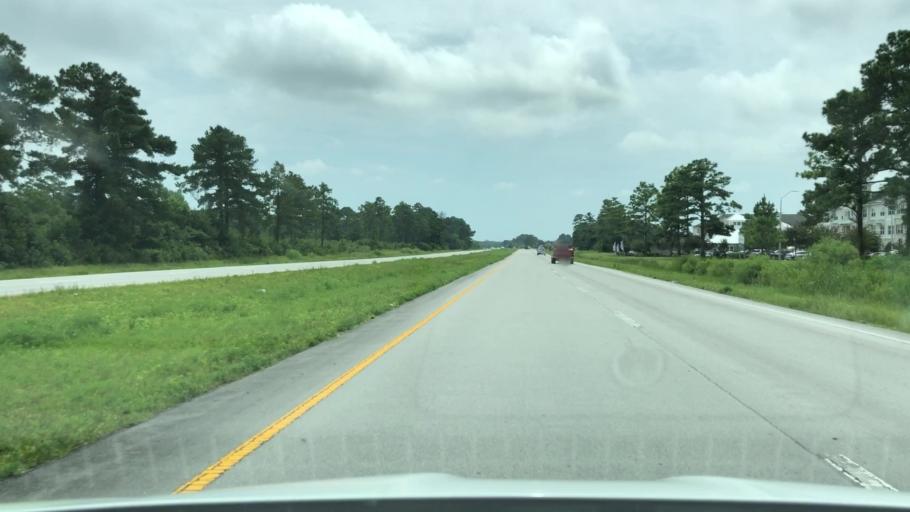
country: US
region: North Carolina
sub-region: Carteret County
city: Newport
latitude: 34.7984
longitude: -76.8780
